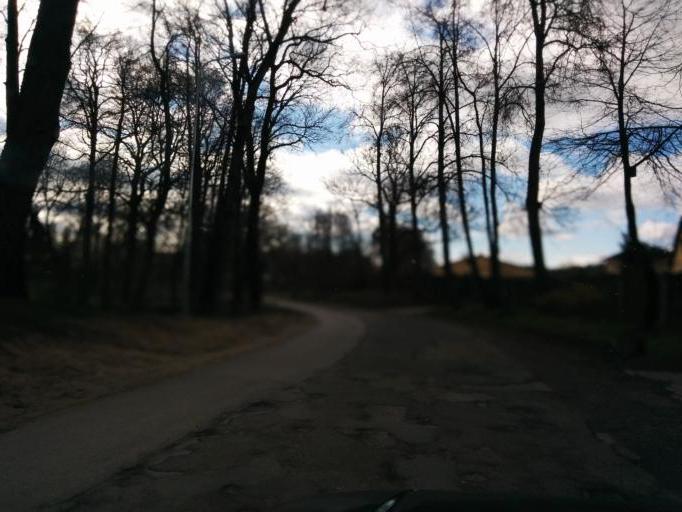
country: LV
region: Kekava
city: Balozi
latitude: 56.8889
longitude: 24.1565
